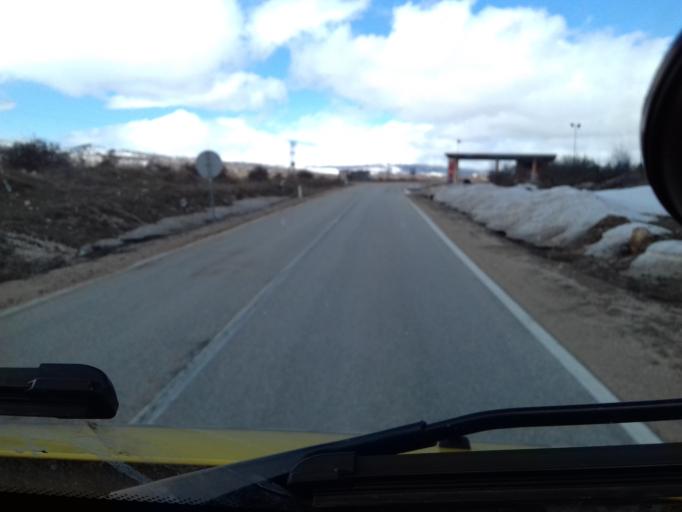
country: BA
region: Federation of Bosnia and Herzegovina
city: Tomislavgrad
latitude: 43.7675
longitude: 17.2360
